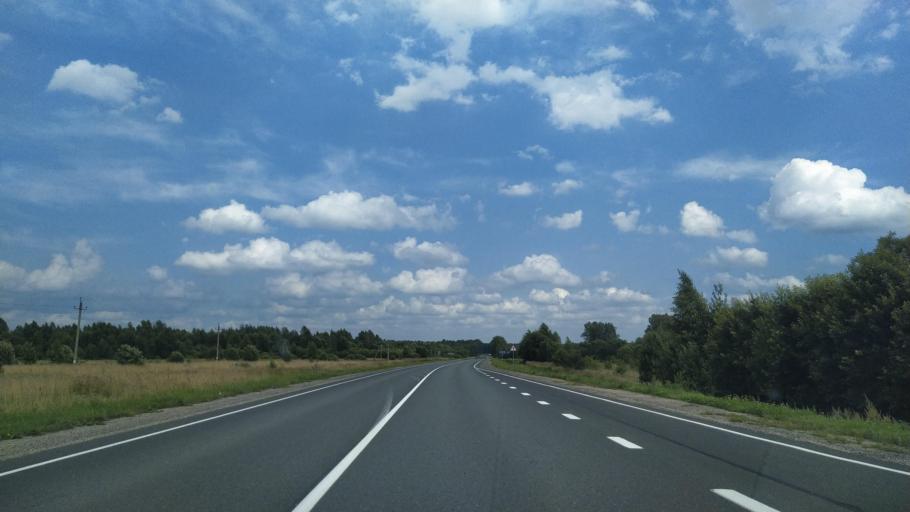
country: RU
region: Pskov
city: Dno
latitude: 57.9833
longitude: 29.7618
